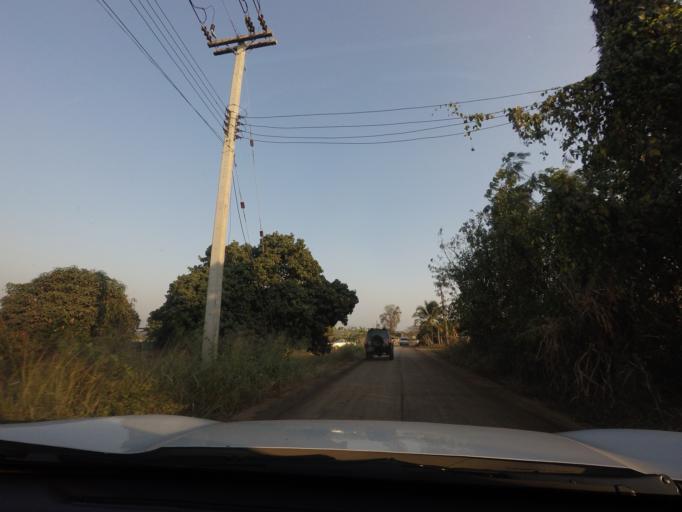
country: TH
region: Nakhon Ratchasima
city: Pak Chong
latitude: 14.6453
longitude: 101.4016
